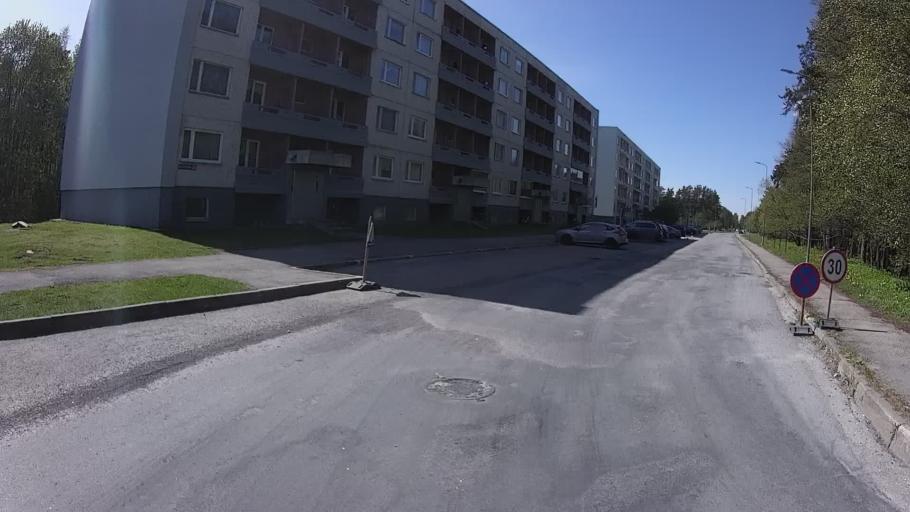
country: EE
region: Laeaene
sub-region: Haapsalu linn
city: Haapsalu
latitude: 58.9348
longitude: 23.5610
